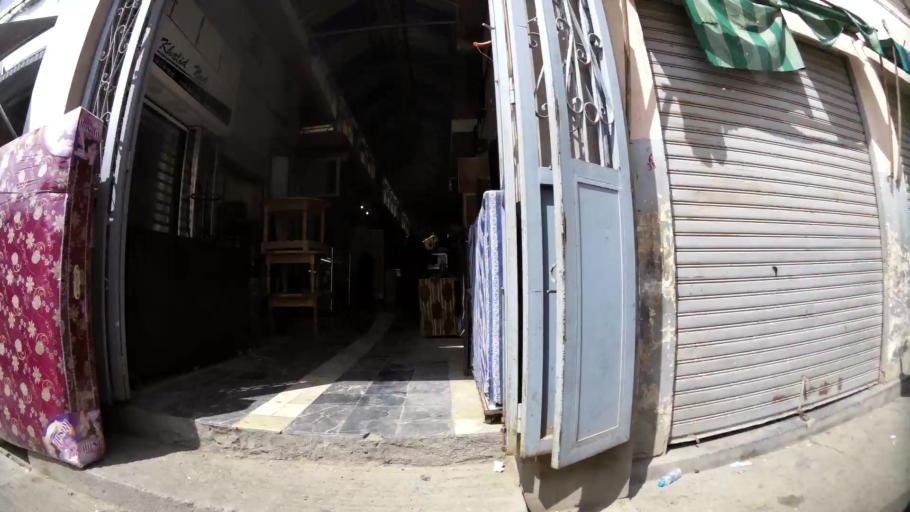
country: MA
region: Oriental
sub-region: Oujda-Angad
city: Oujda
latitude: 34.6809
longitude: -1.9081
